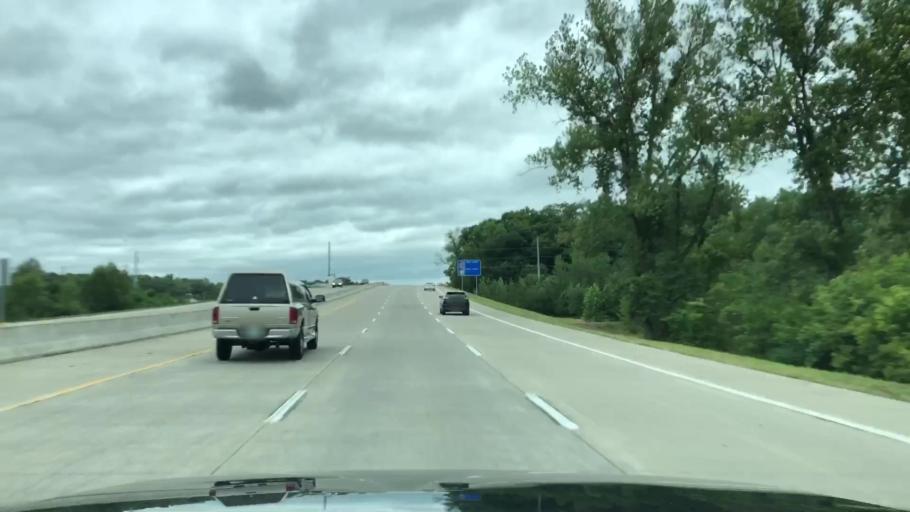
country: US
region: Missouri
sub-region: Saint Louis County
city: Maryland Heights
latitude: 38.6946
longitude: -90.5018
